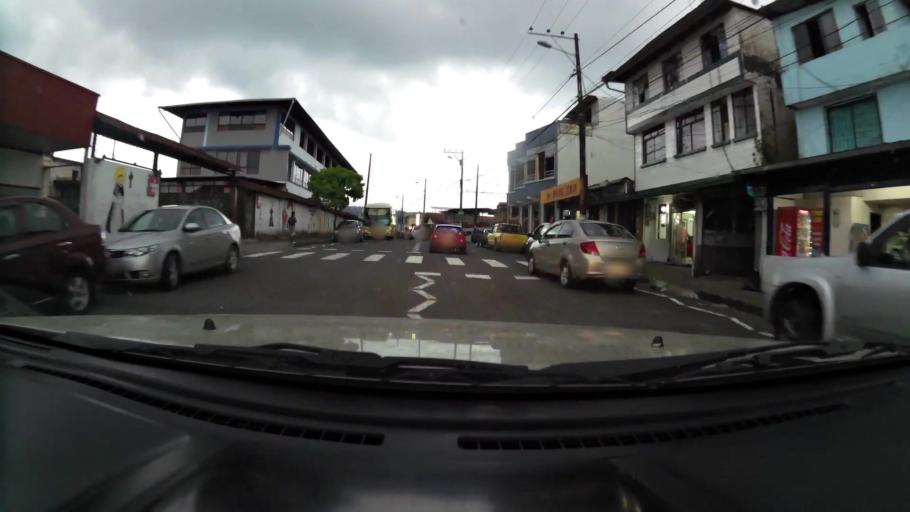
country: EC
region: Pastaza
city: Puyo
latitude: -1.4852
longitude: -78.0041
